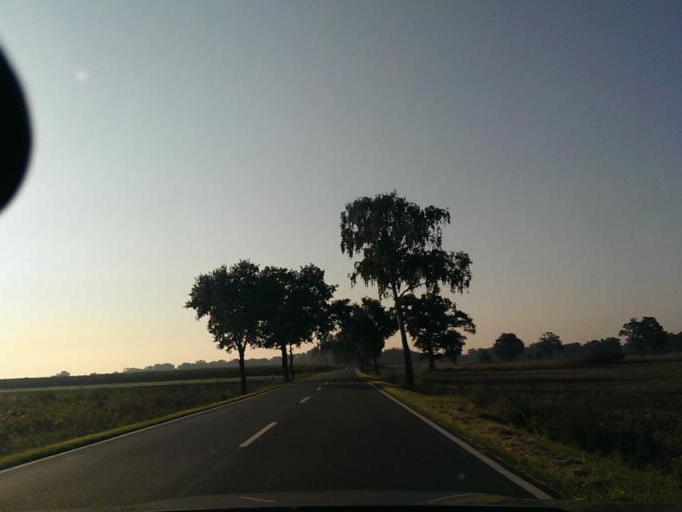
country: DE
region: Lower Saxony
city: Elze
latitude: 52.5735
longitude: 9.7498
